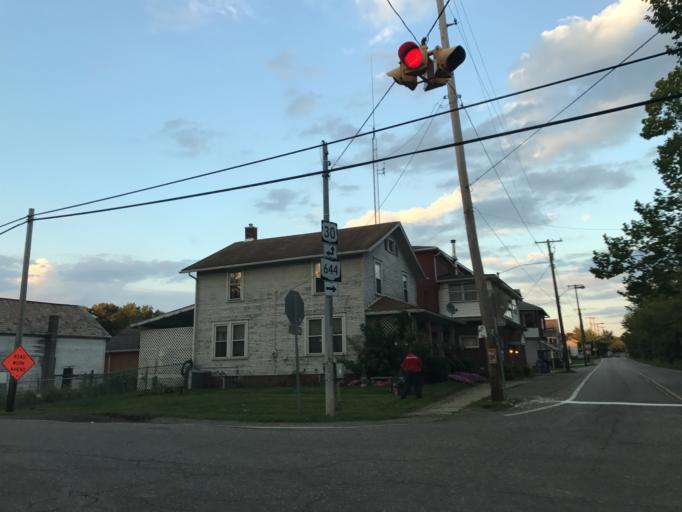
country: US
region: Ohio
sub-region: Stark County
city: Minerva
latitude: 40.7354
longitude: -80.9560
